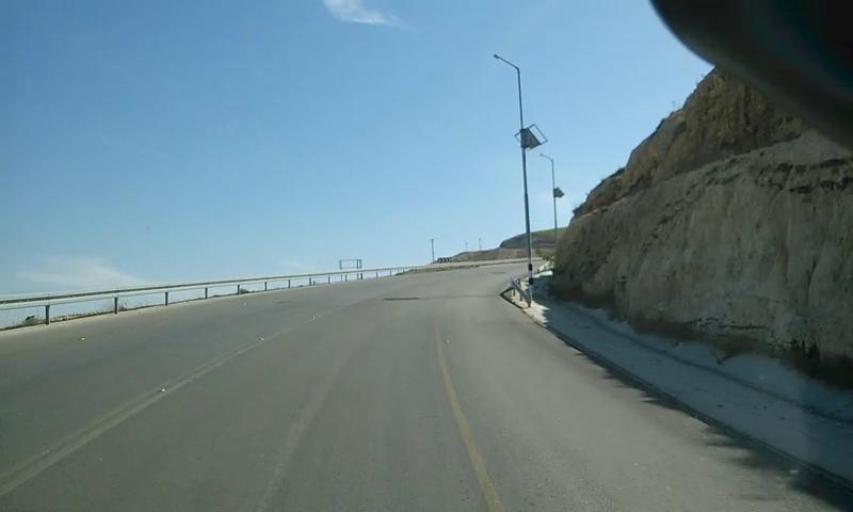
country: PS
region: West Bank
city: Al `Ayzariyah
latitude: 31.7504
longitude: 35.2952
